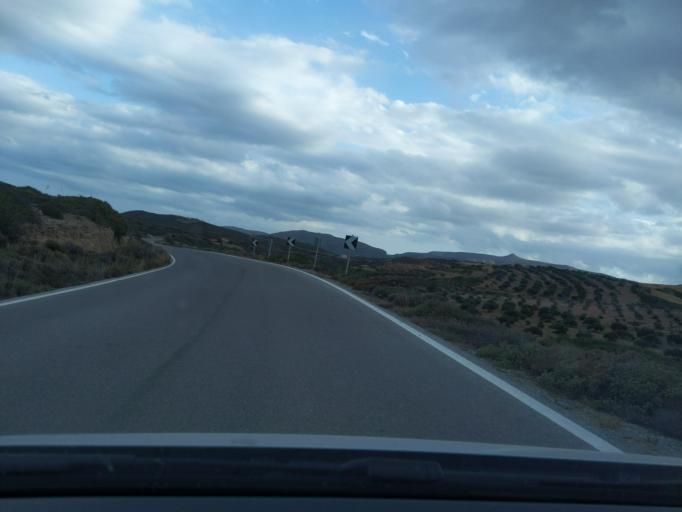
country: GR
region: Crete
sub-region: Nomos Lasithiou
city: Palekastro
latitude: 35.2313
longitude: 26.2527
